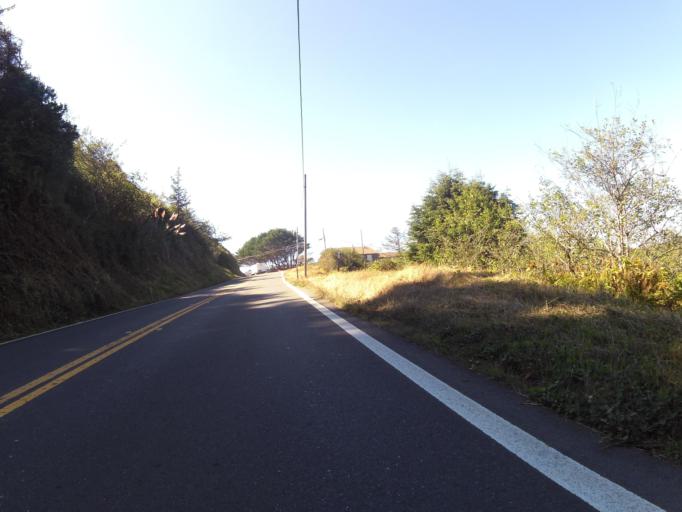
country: US
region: California
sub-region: Mendocino County
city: Fort Bragg
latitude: 39.6480
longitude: -123.7818
